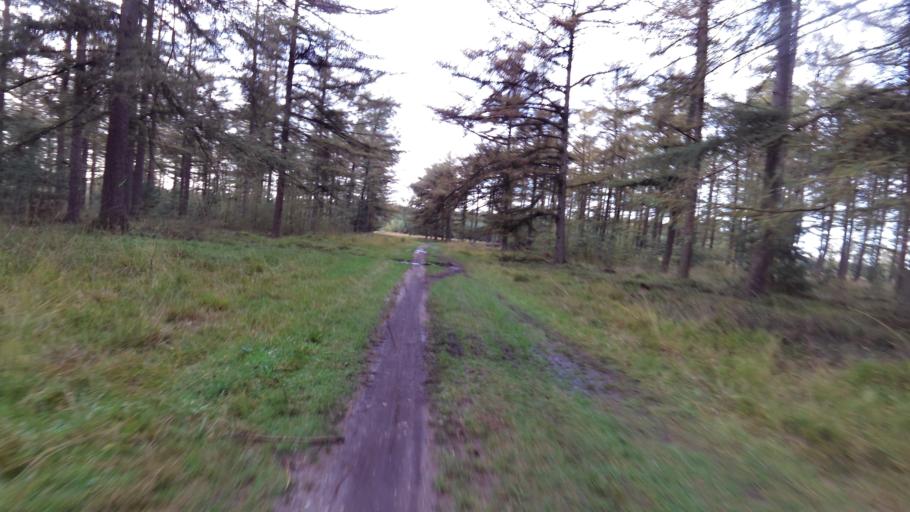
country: NL
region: Gelderland
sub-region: Gemeente Renkum
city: Wolfheze
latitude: 52.0315
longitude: 5.8044
